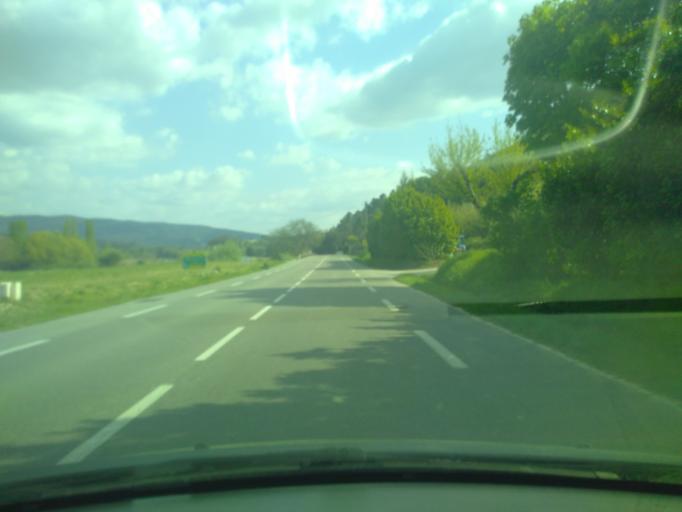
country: FR
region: Provence-Alpes-Cote d'Azur
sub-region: Departement du Vaucluse
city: Malaucene
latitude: 44.2064
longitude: 5.1056
